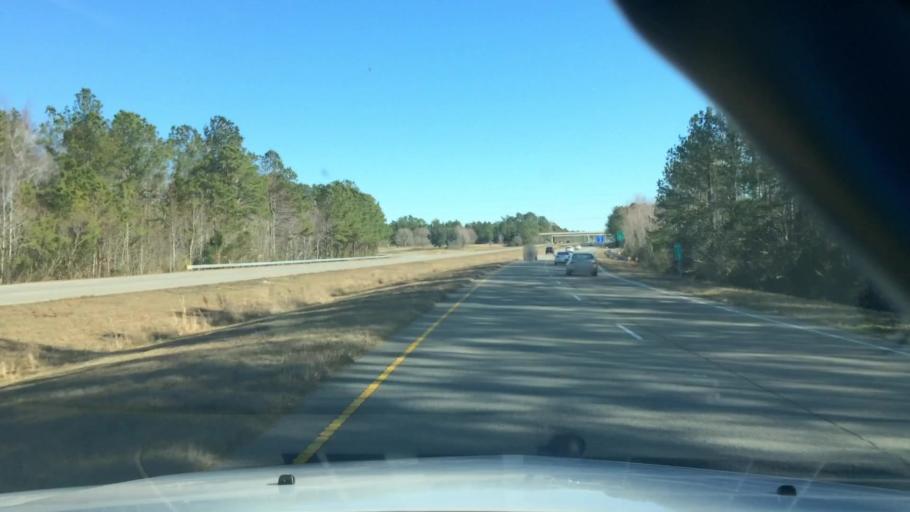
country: US
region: North Carolina
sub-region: Brunswick County
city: Shallotte
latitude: 33.9725
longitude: -78.4094
